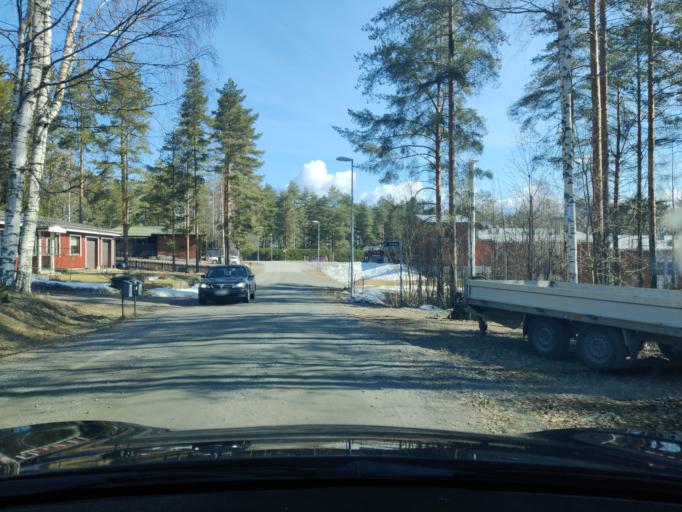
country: FI
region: Northern Savo
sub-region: Kuopio
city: Vehmersalmi
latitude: 62.7592
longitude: 28.0353
